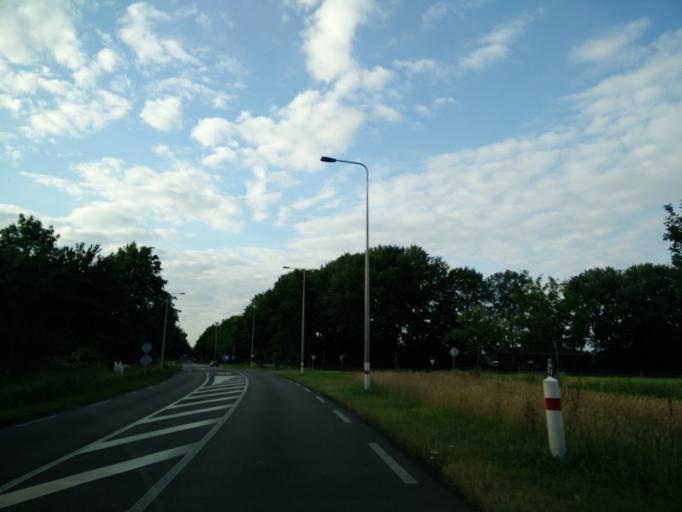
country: NL
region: Utrecht
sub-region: Gemeente Utrechtse Heuvelrug
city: Maarsbergen
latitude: 52.0664
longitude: 5.4096
